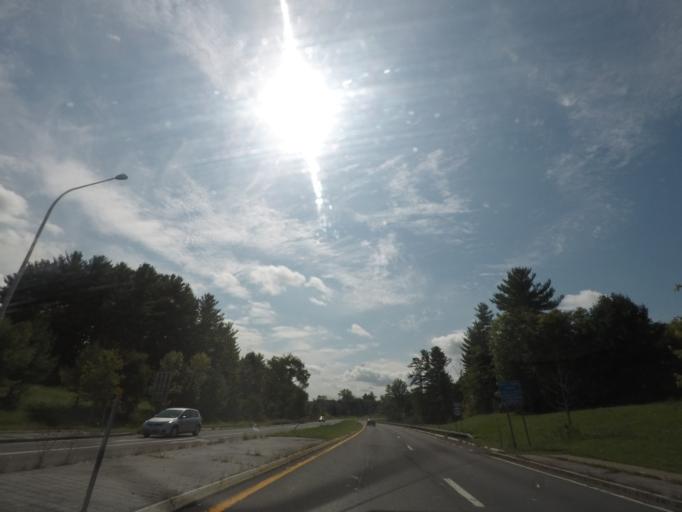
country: US
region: New York
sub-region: Albany County
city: Delmar
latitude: 42.6447
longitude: -73.8531
